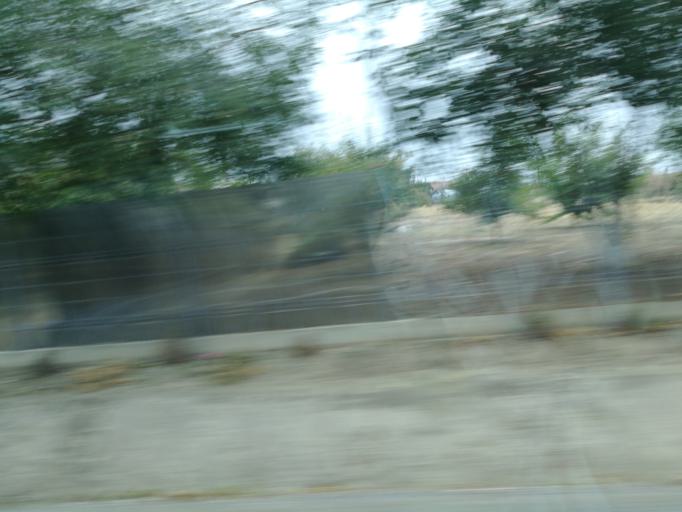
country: RO
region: Tulcea
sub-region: Comuna Horia
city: Horia
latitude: 45.0211
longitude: 28.4482
